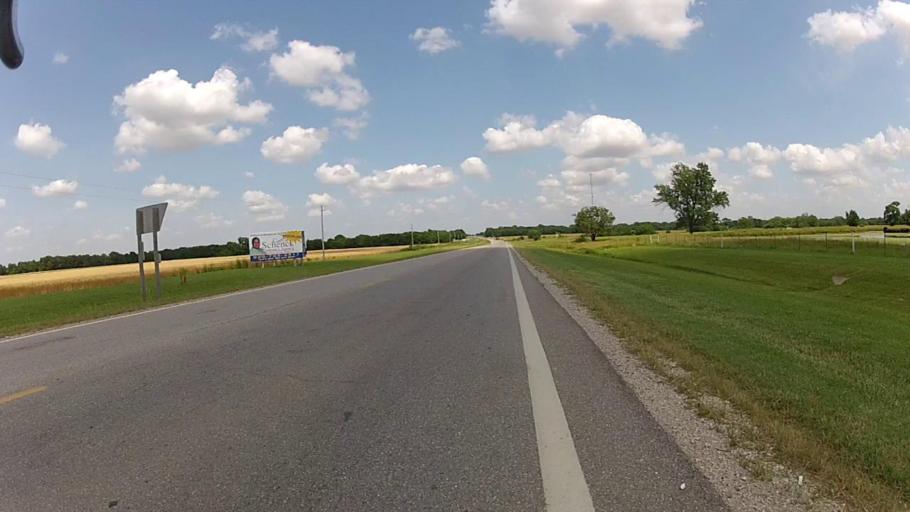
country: US
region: Kansas
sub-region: Labette County
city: Altamont
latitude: 37.1928
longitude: -95.2840
